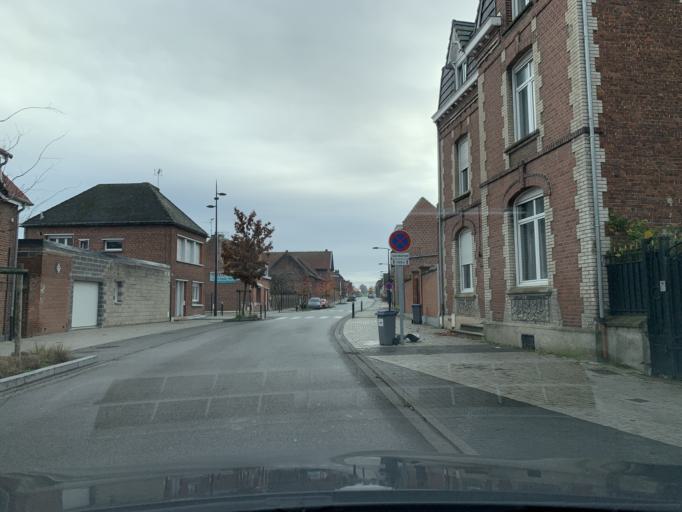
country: FR
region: Nord-Pas-de-Calais
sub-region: Departement du Nord
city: Cantin
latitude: 50.3102
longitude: 3.1265
